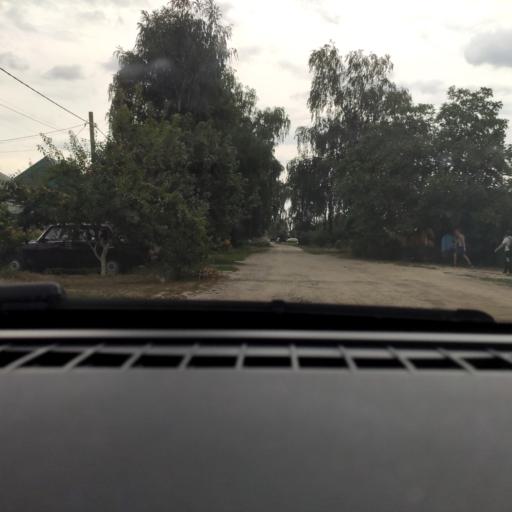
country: RU
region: Voronezj
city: Maslovka
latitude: 51.6311
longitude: 39.2677
